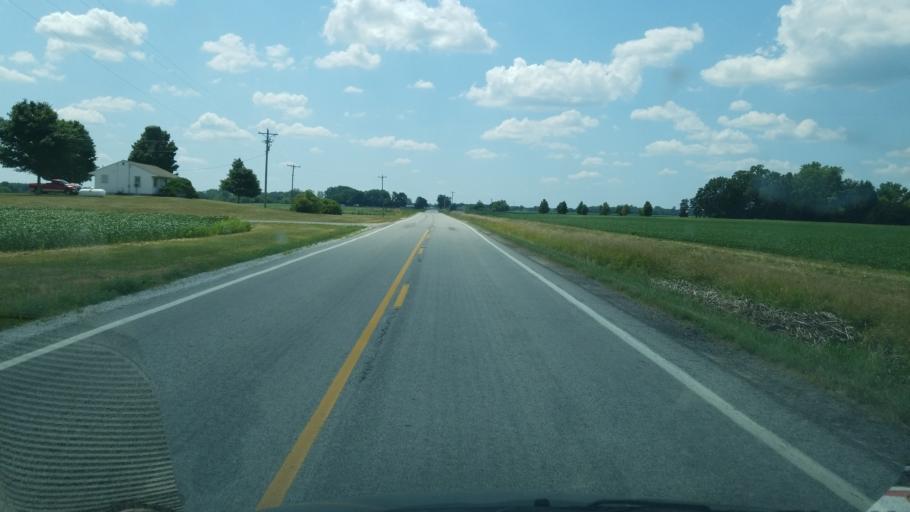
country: US
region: Ohio
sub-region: Champaign County
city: Mechanicsburg
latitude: 40.1440
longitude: -83.5206
